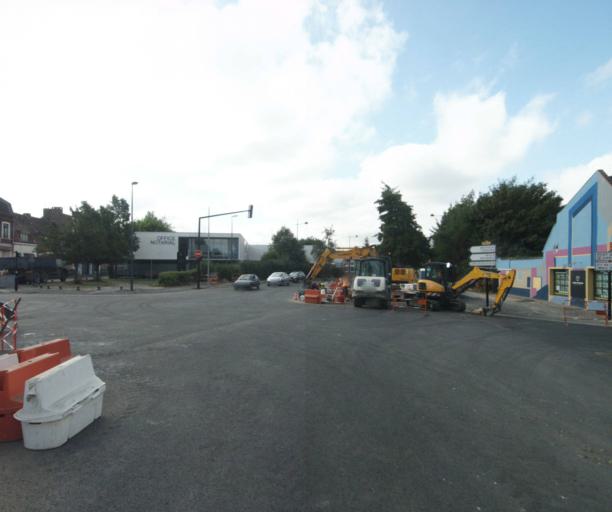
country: FR
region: Nord-Pas-de-Calais
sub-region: Departement du Nord
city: Villeneuve-d'Ascq
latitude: 50.6260
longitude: 3.1537
